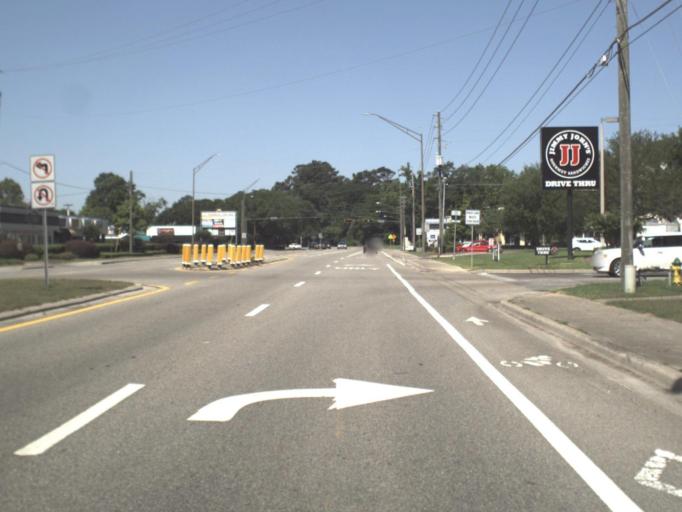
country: US
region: Florida
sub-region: Leon County
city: Tallahassee
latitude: 30.5049
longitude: -84.2524
